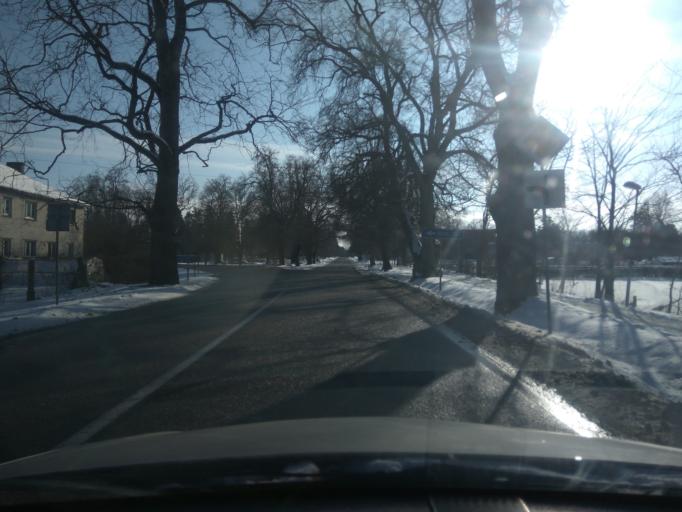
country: LV
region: Kuldigas Rajons
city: Kuldiga
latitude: 57.2780
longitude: 22.0217
